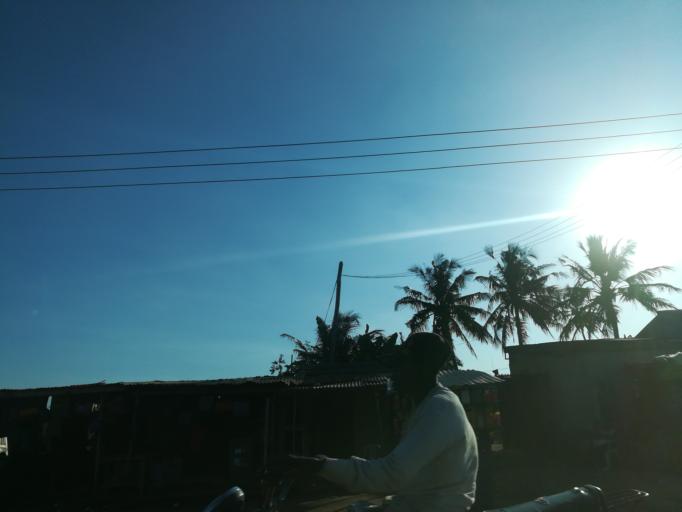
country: NG
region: Lagos
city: Ikorodu
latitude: 6.5850
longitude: 3.5239
